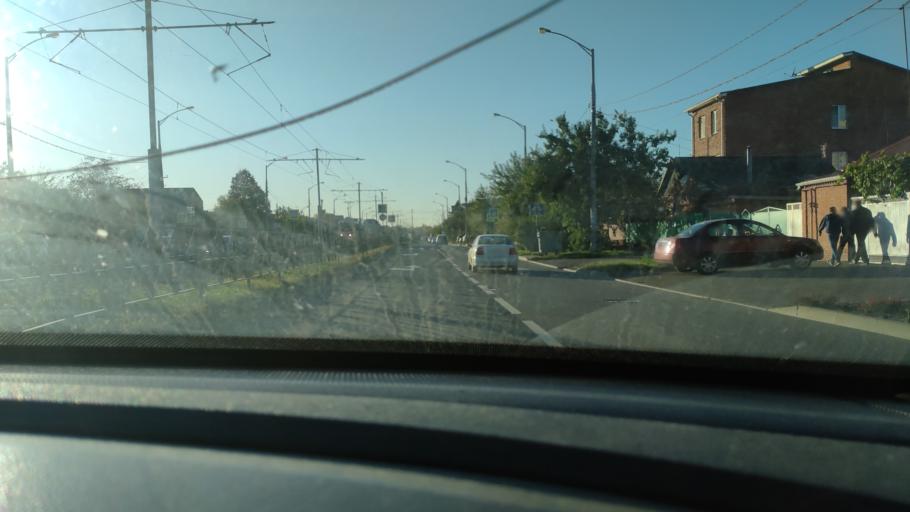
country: RU
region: Krasnodarskiy
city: Krasnodar
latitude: 45.0417
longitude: 38.9462
